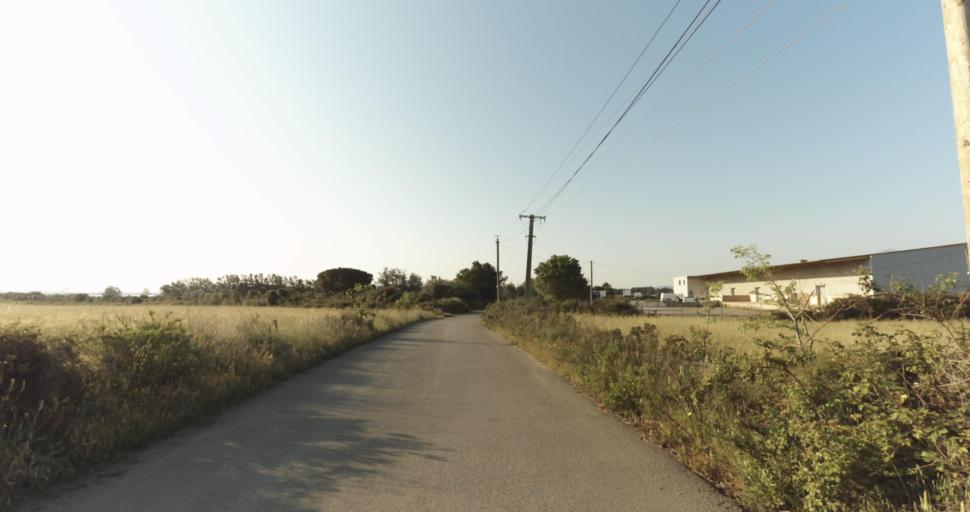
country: FR
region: Corsica
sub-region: Departement de la Haute-Corse
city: Biguglia
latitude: 42.6050
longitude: 9.4523
